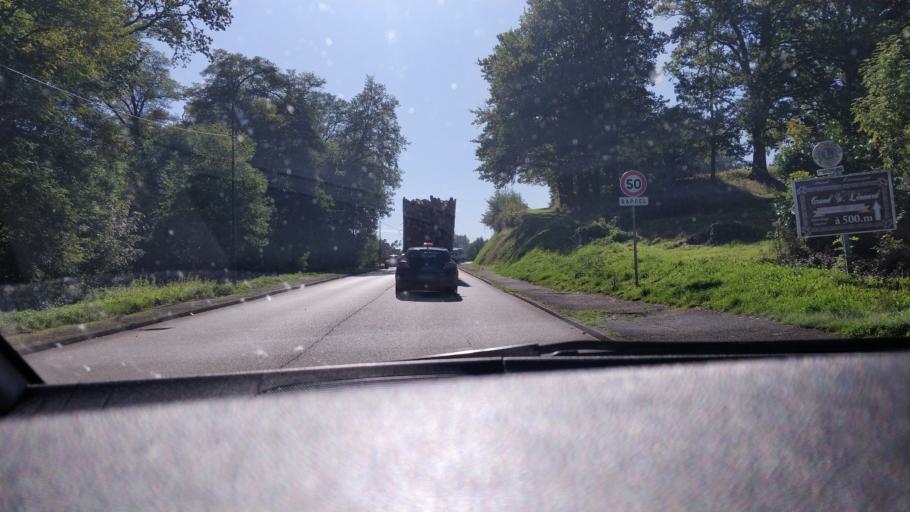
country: FR
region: Limousin
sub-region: Departement de la Haute-Vienne
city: Saint-Leonard-de-Noblat
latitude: 45.8430
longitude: 1.4930
